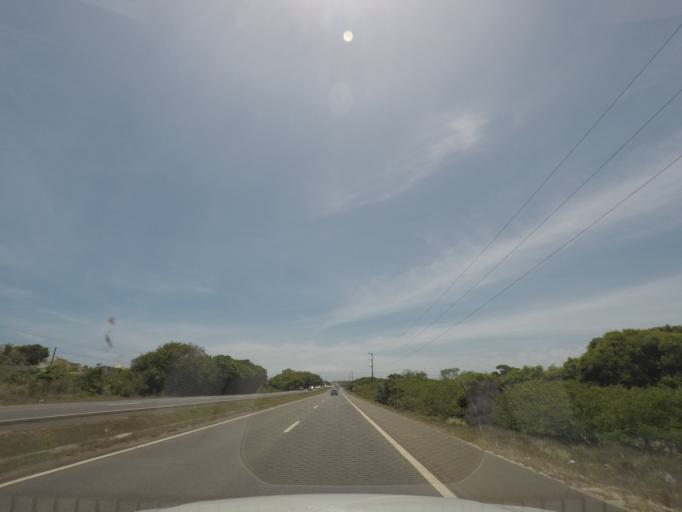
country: BR
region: Bahia
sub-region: Camacari
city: Camacari
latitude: -12.6836
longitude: -38.1095
